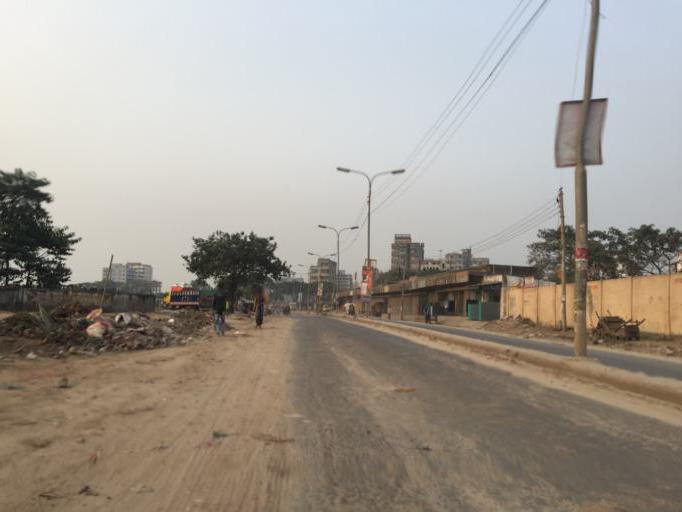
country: BD
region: Dhaka
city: Azimpur
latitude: 23.7961
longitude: 90.3475
